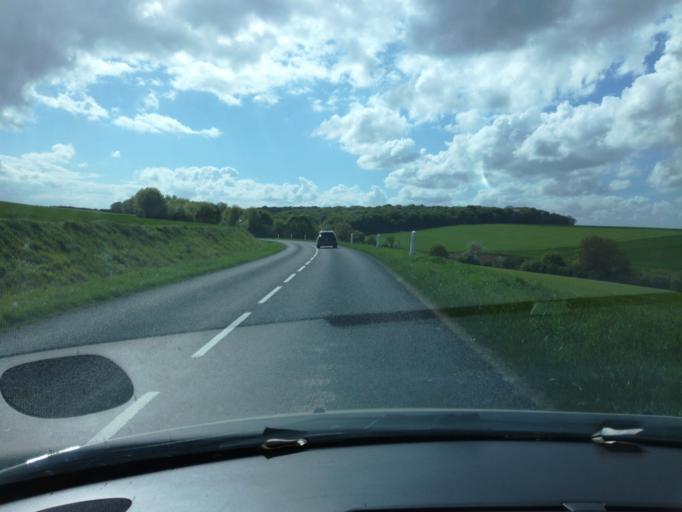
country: FR
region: Picardie
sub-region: Departement de la Somme
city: Picquigny
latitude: 49.8898
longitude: 2.1089
